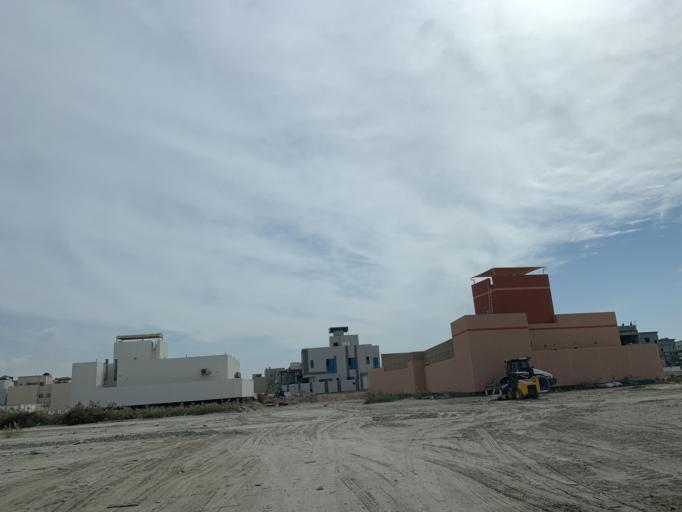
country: BH
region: Central Governorate
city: Madinat Hamad
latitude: 26.1091
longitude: 50.4722
